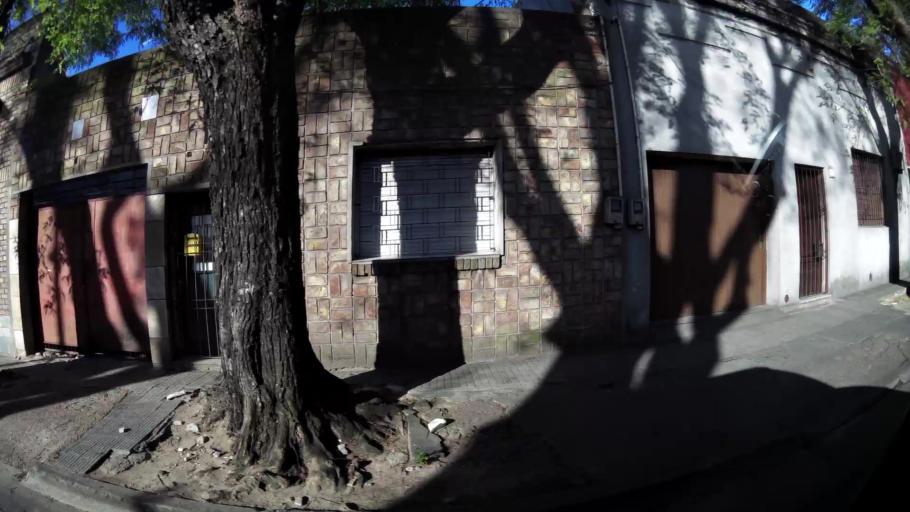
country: UY
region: Montevideo
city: Montevideo
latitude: -34.8719
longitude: -56.1346
